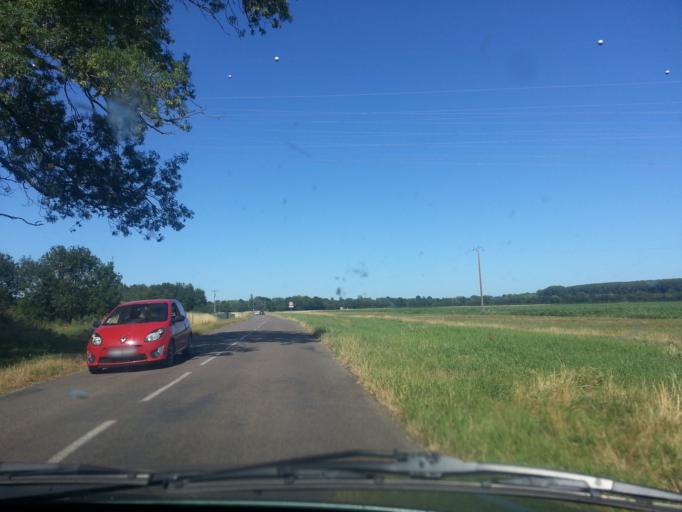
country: FR
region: Bourgogne
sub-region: Departement de Saone-et-Loire
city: Saint-Marcel
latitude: 46.7861
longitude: 4.8778
